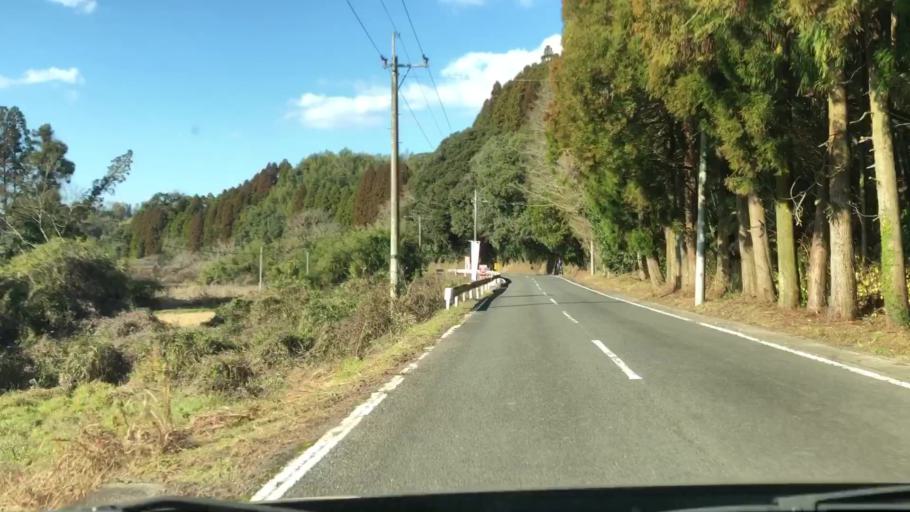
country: JP
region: Kagoshima
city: Satsumasendai
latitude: 31.8567
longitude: 130.3605
